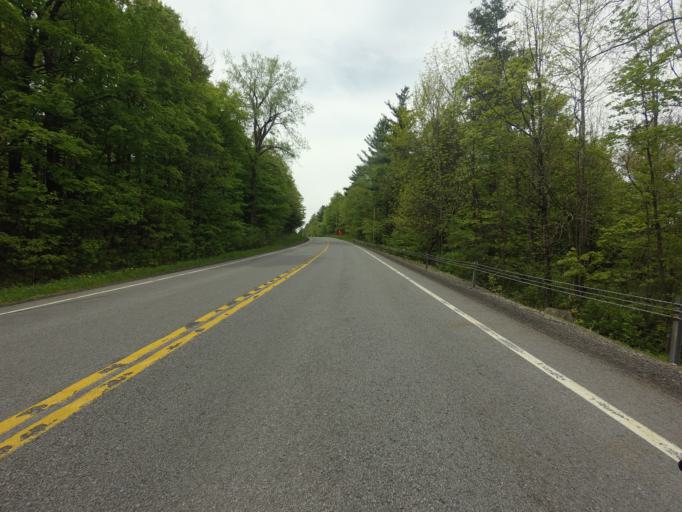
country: US
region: New York
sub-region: St. Lawrence County
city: Hannawa Falls
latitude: 44.6391
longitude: -74.7907
